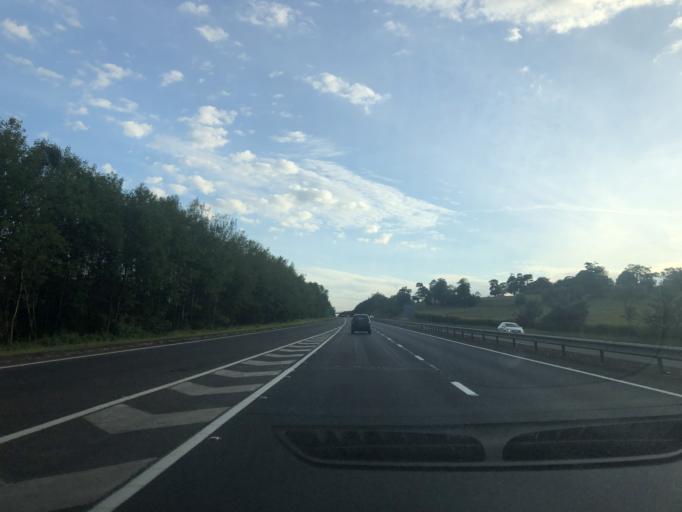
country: GB
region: Scotland
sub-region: Fife
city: Lochgelly
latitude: 56.1212
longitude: -3.2946
